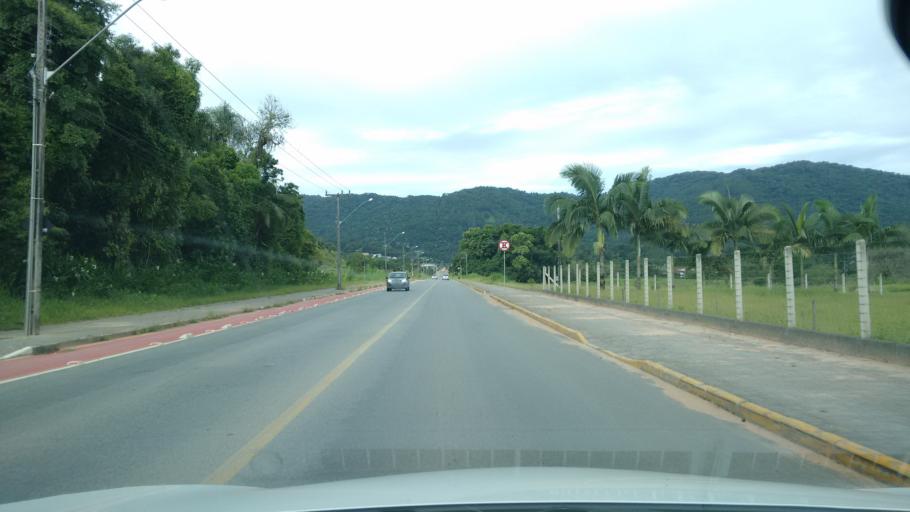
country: BR
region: Santa Catarina
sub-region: Timbo
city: Timbo
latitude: -26.8086
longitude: -49.2593
